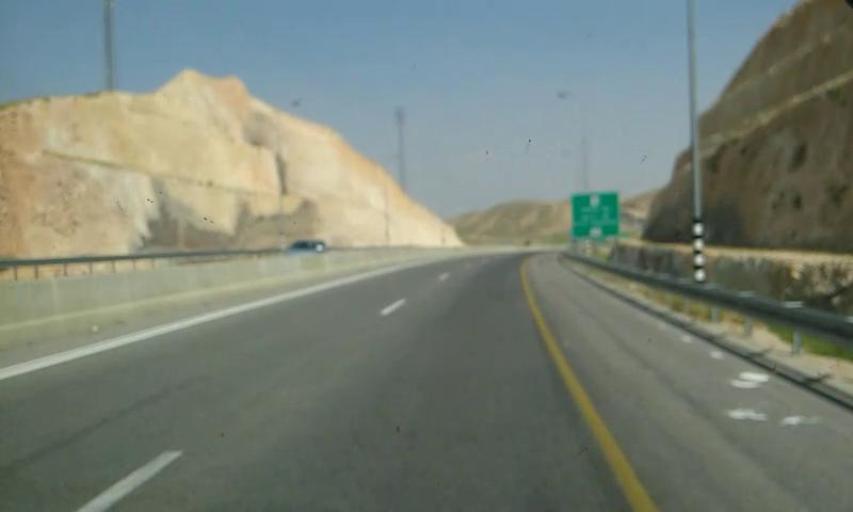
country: PS
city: Az Za`ayyim
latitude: 31.8135
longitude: 35.3450
